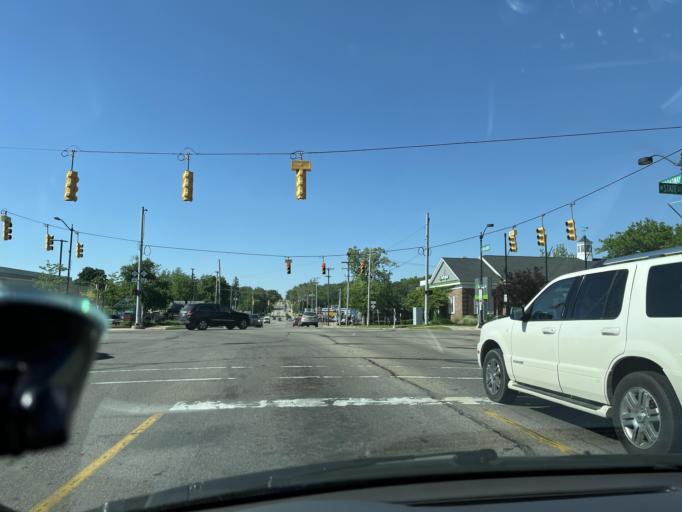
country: US
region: Michigan
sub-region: Barry County
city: Hastings
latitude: 42.6484
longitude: -85.2907
